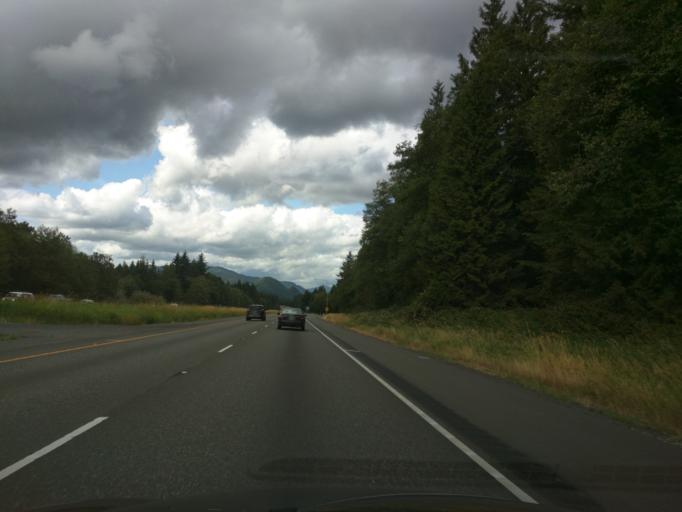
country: US
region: Washington
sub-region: Skagit County
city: Burlington
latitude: 48.5760
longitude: -122.3470
